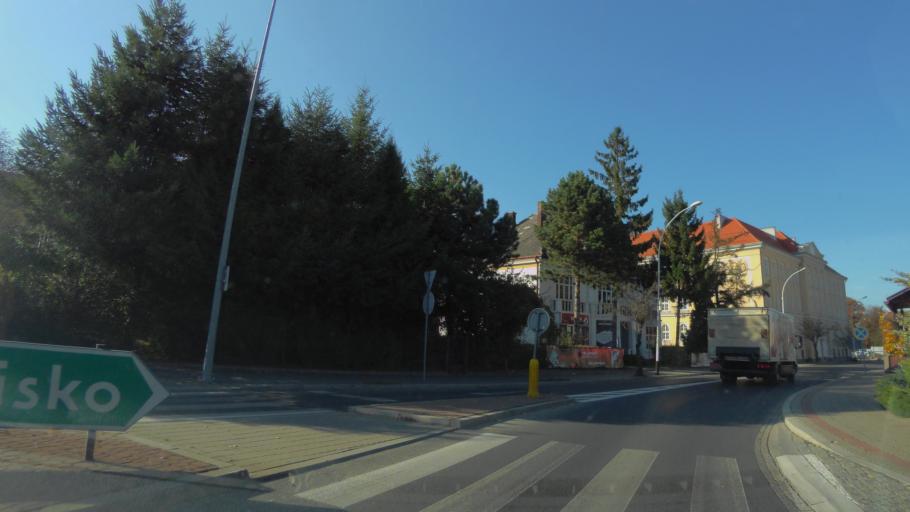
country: PL
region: Subcarpathian Voivodeship
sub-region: Powiat lezajski
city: Lezajsk
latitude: 50.2576
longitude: 22.4214
